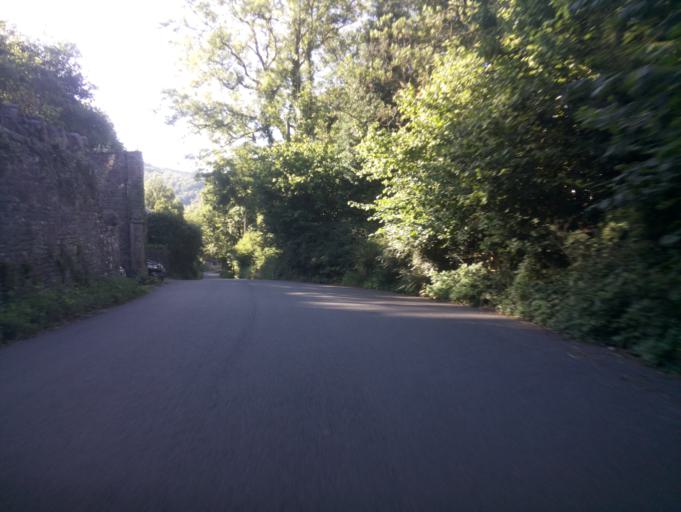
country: GB
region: Wales
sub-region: Monmouthshire
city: Tintern
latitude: 51.7062
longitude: -2.6838
